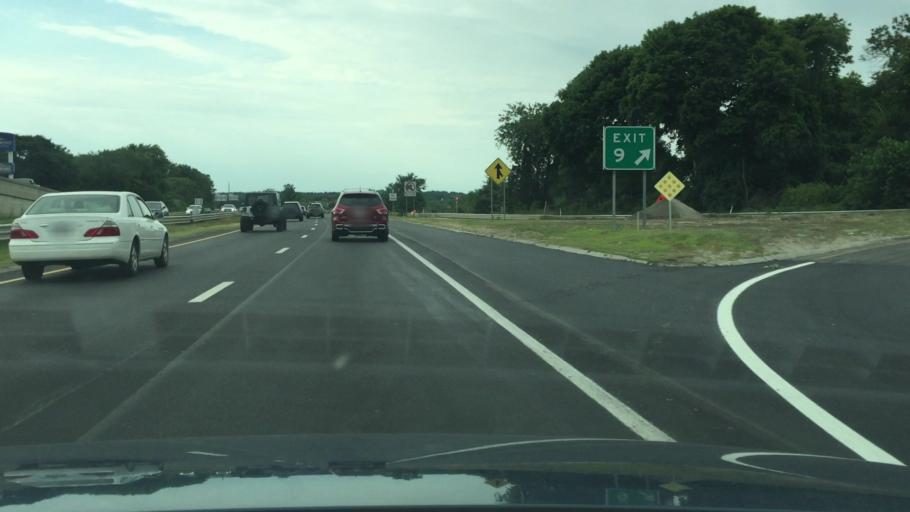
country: US
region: Massachusetts
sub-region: Plymouth County
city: Kingston
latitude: 41.9888
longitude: -70.7175
